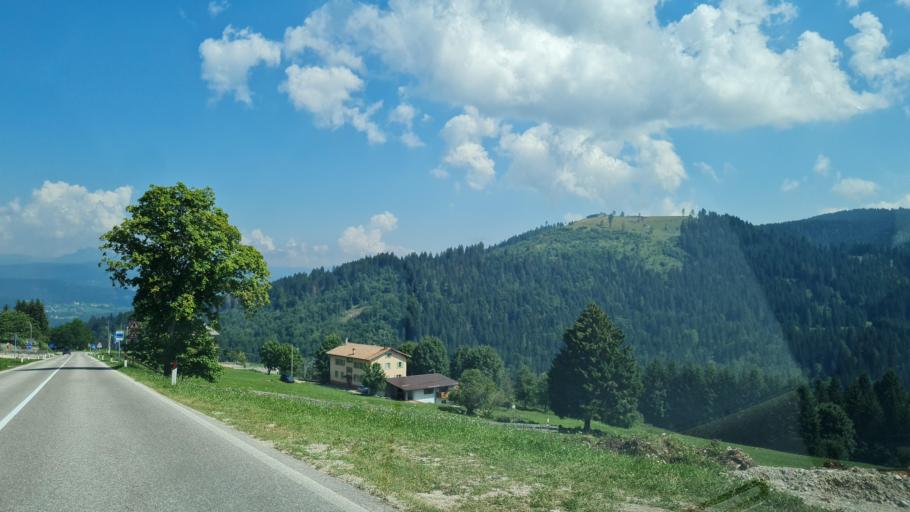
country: IT
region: Trentino-Alto Adige
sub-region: Provincia di Trento
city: Folgaria
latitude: 45.9243
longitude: 11.2123
